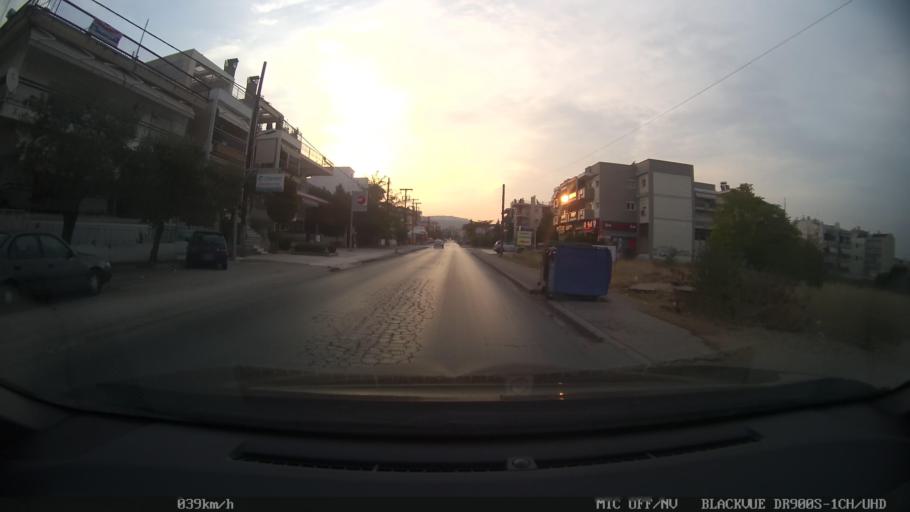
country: GR
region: Central Macedonia
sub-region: Nomos Thessalonikis
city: Pylaia
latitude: 40.6095
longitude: 22.9903
